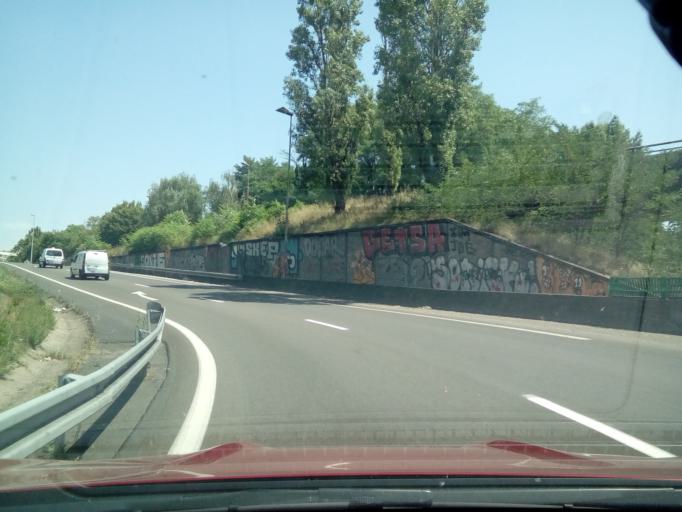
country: FR
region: Rhone-Alpes
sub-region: Departement du Rhone
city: Bron
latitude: 45.7273
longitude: 4.8966
